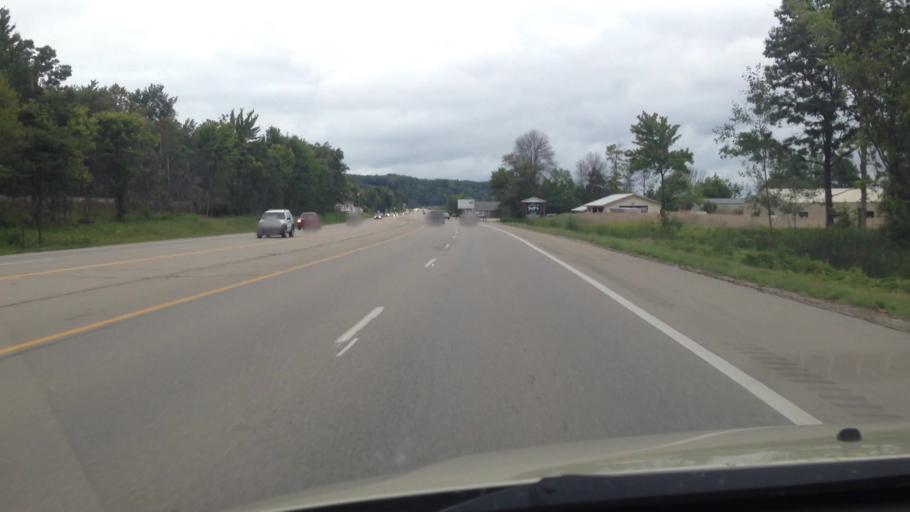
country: US
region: Michigan
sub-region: Delta County
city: Gladstone
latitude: 45.8082
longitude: -87.0603
